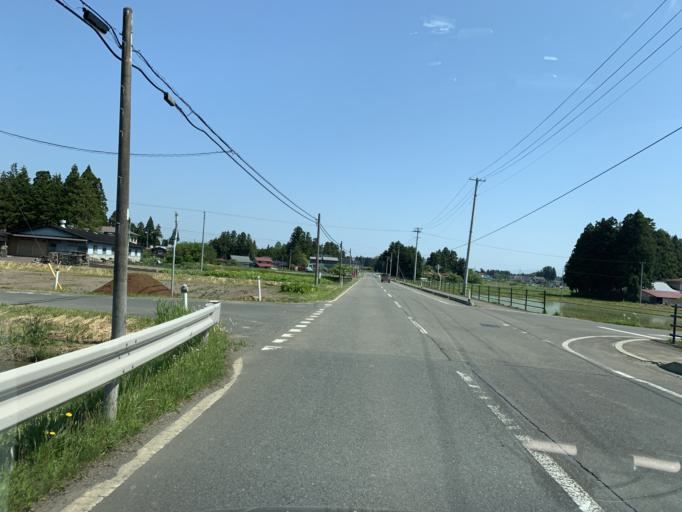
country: JP
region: Iwate
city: Mizusawa
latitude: 39.0927
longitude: 141.0740
